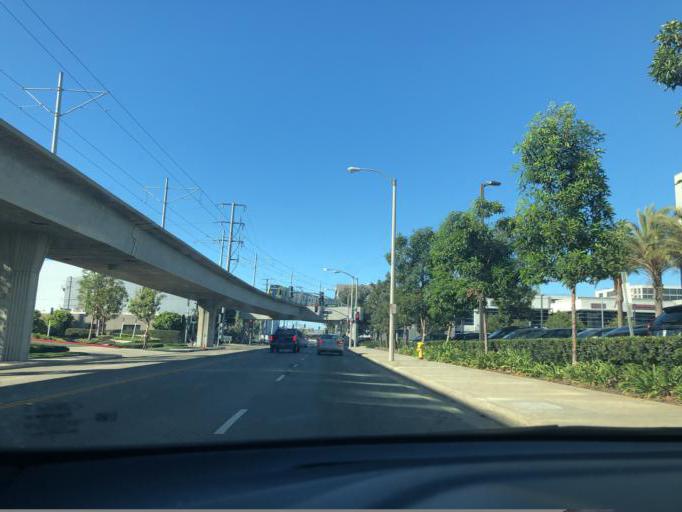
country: US
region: California
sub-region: Los Angeles County
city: Del Aire
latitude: 33.9260
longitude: -118.3874
